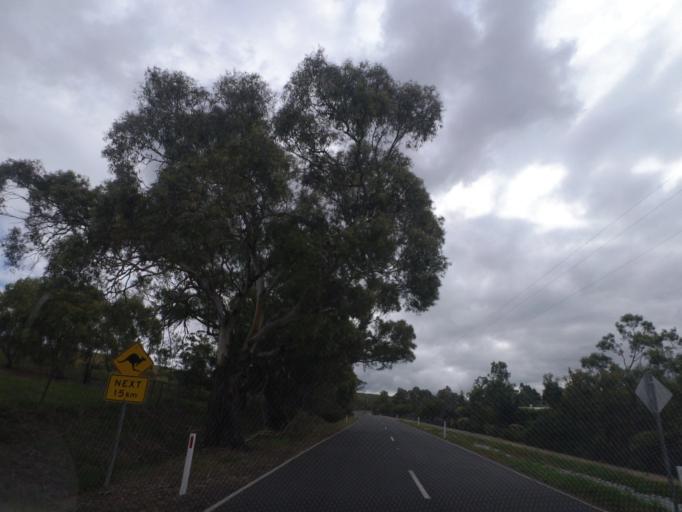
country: AU
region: Victoria
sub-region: Whittlesea
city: Whittlesea
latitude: -37.5254
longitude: 145.1106
